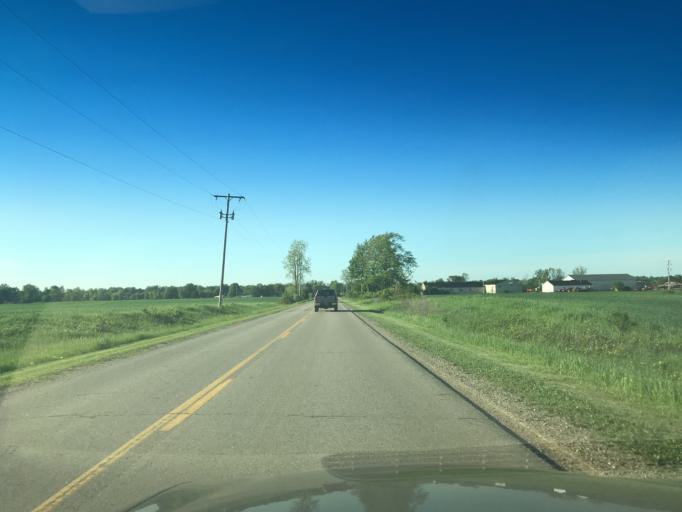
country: US
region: Michigan
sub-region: Ingham County
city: Mason
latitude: 42.5610
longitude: -84.4530
